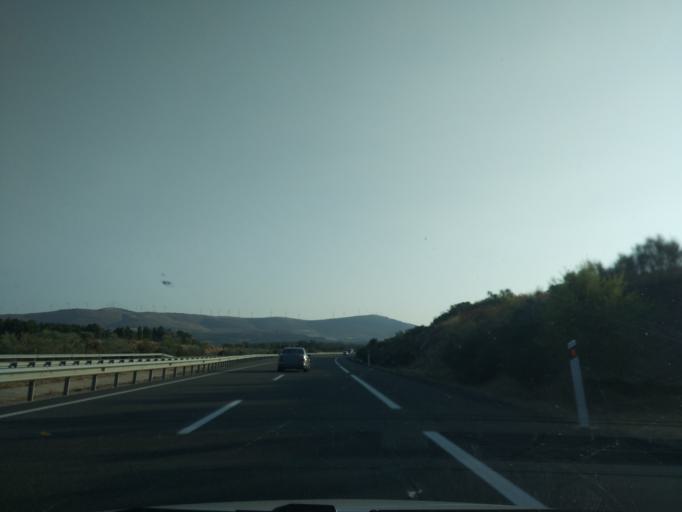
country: ES
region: Castille and Leon
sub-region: Provincia de Segovia
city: Villacastin
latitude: 40.7628
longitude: -4.4408
